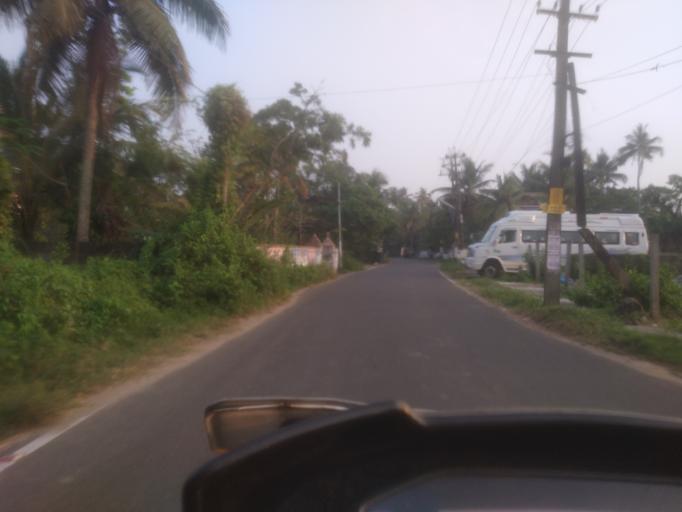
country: IN
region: Kerala
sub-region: Ernakulam
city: Cochin
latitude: 10.0033
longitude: 76.2217
